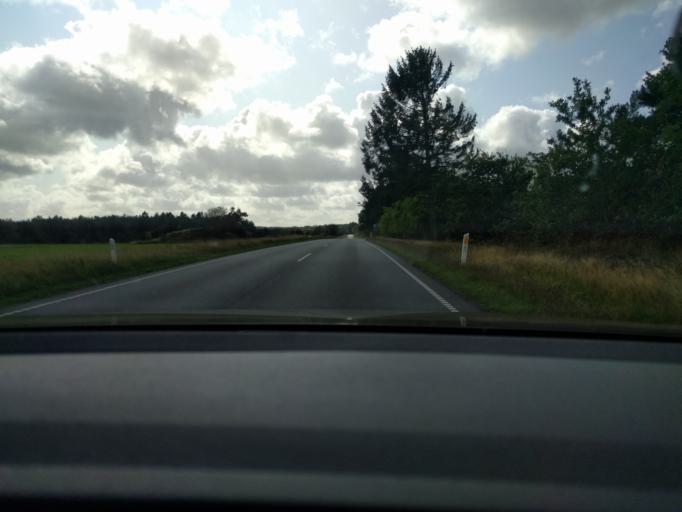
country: DK
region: Central Jutland
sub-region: Viborg Kommune
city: Bjerringbro
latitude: 56.2915
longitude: 9.6572
